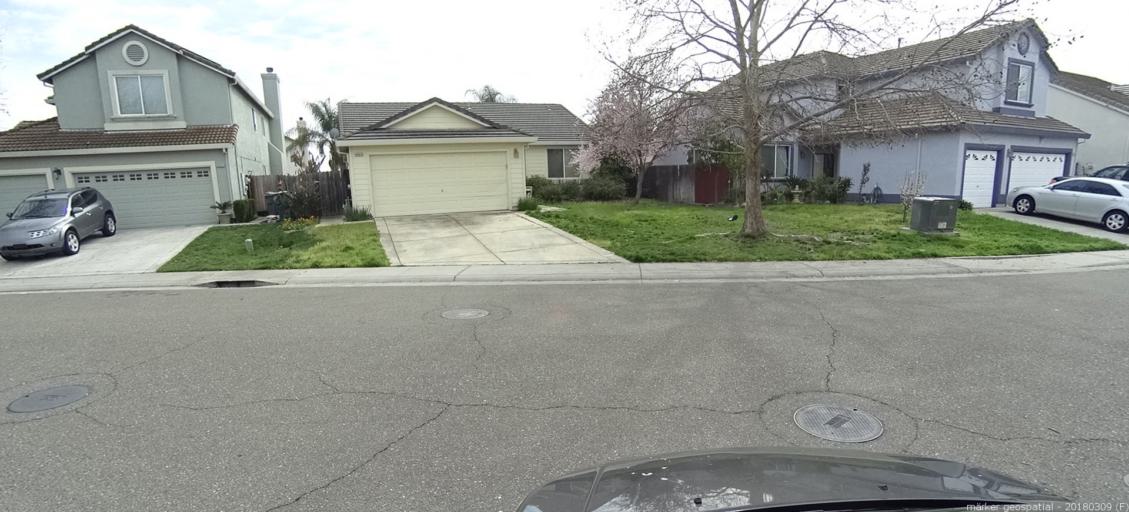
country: US
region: California
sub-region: Sacramento County
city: Vineyard
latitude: 38.4585
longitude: -121.3692
